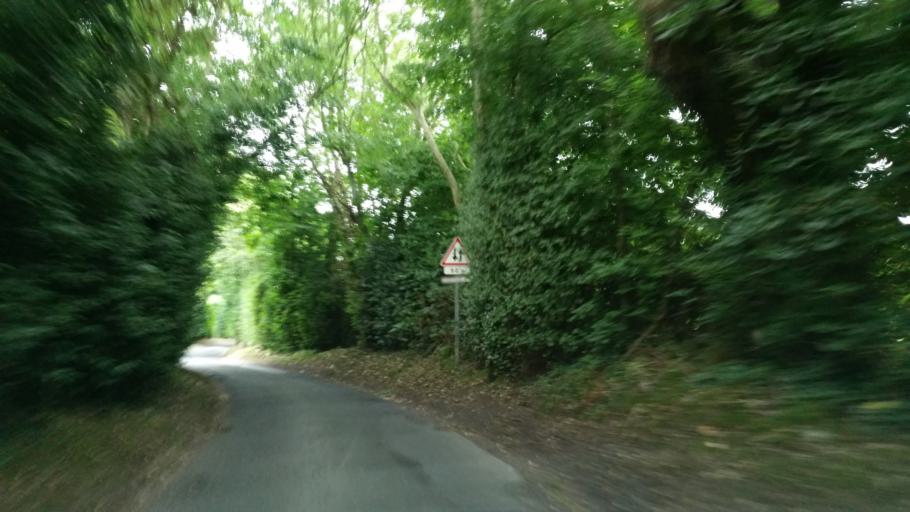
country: FR
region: Lower Normandy
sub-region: Departement du Calvados
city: Honfleur
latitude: 49.4058
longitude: 0.2327
